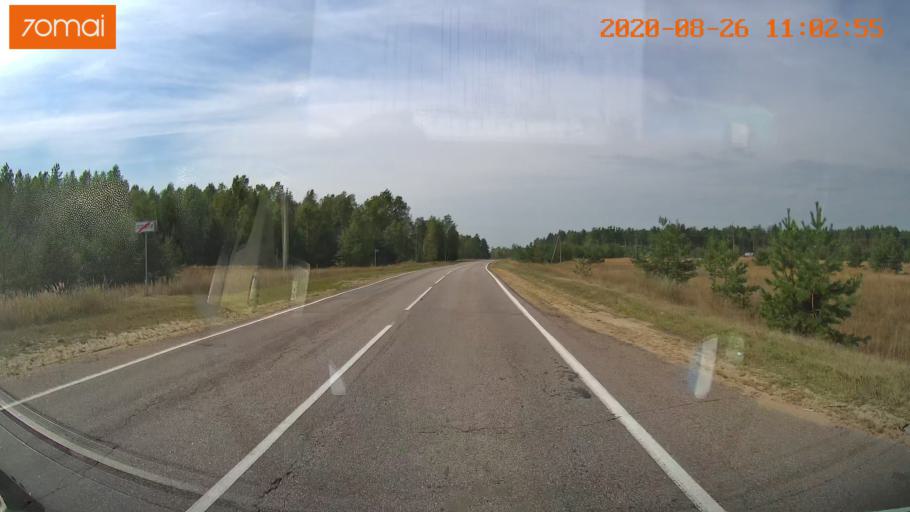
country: RU
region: Rjazan
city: Izhevskoye
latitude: 54.5452
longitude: 41.2203
